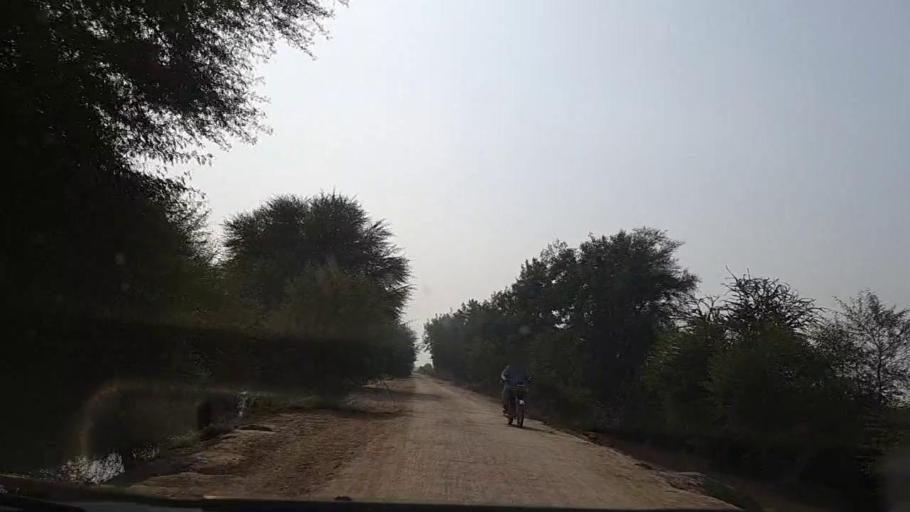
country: PK
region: Sindh
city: Sanghar
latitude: 26.0342
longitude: 68.9770
